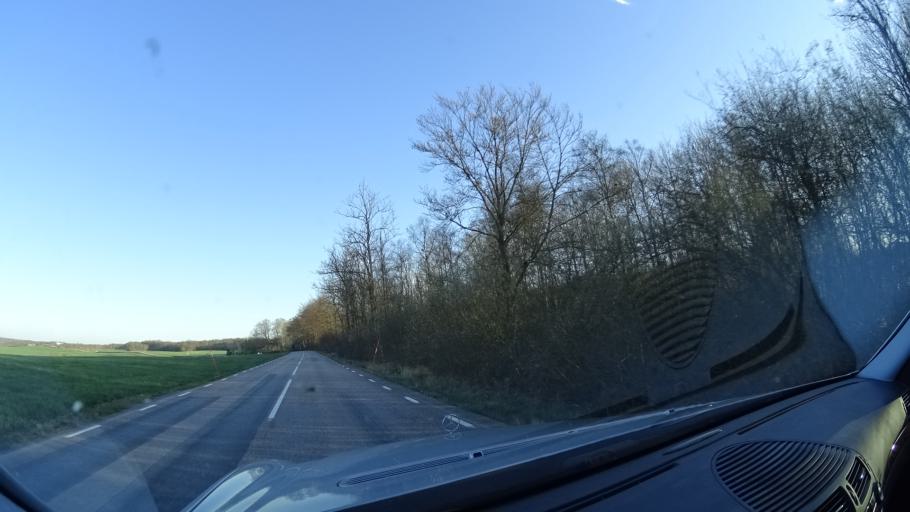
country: SE
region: Skane
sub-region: Bjuvs Kommun
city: Billesholm
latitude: 56.0235
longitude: 13.0465
